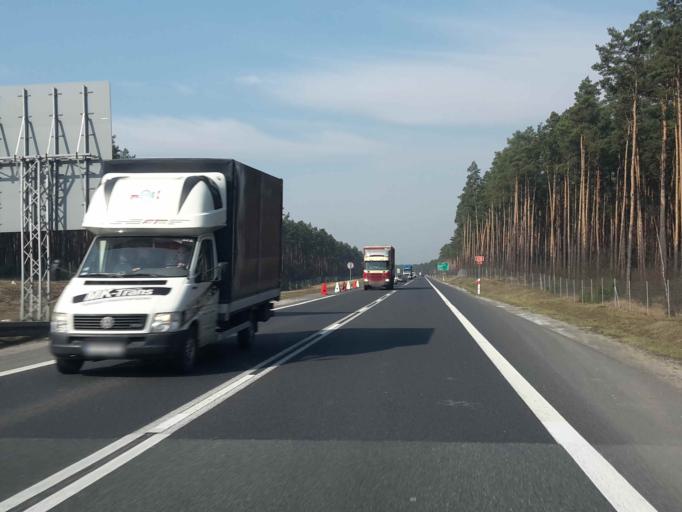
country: PL
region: Kujawsko-Pomorskie
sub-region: Torun
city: Torun
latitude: 52.9690
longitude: 18.6657
